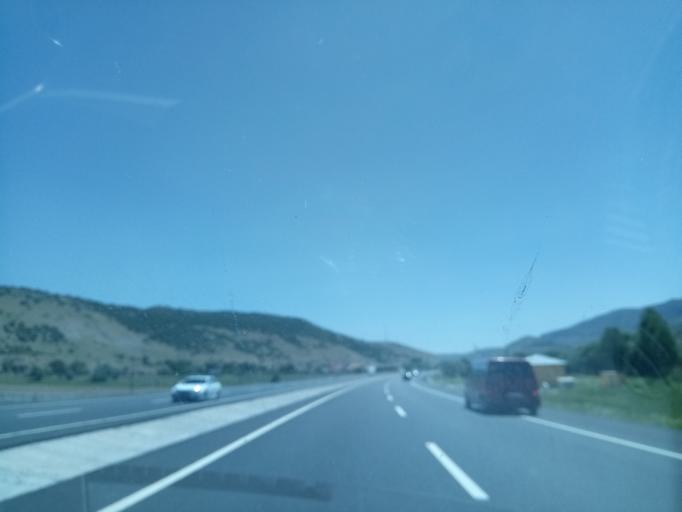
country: TR
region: Konya
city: Kiziloren
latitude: 37.7510
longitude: 32.0958
